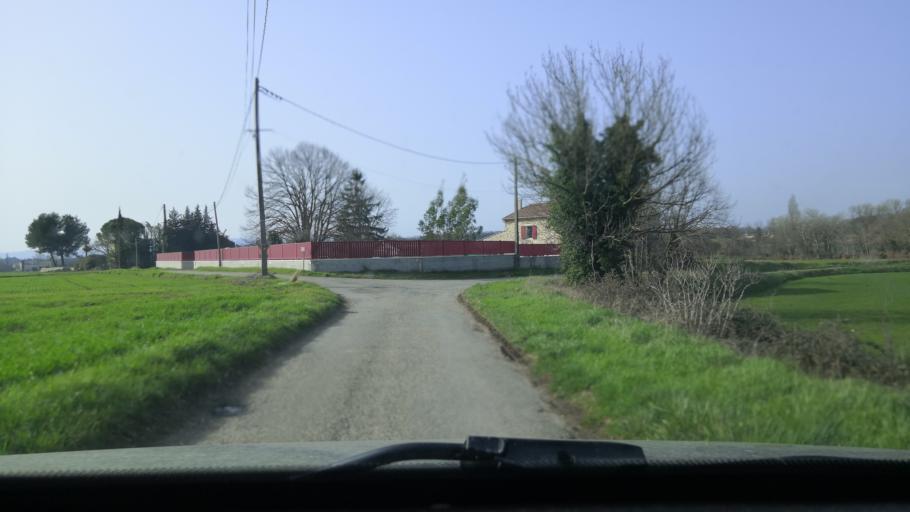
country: FR
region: Rhone-Alpes
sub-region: Departement de la Drome
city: Montboucher-sur-Jabron
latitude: 44.5582
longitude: 4.8613
